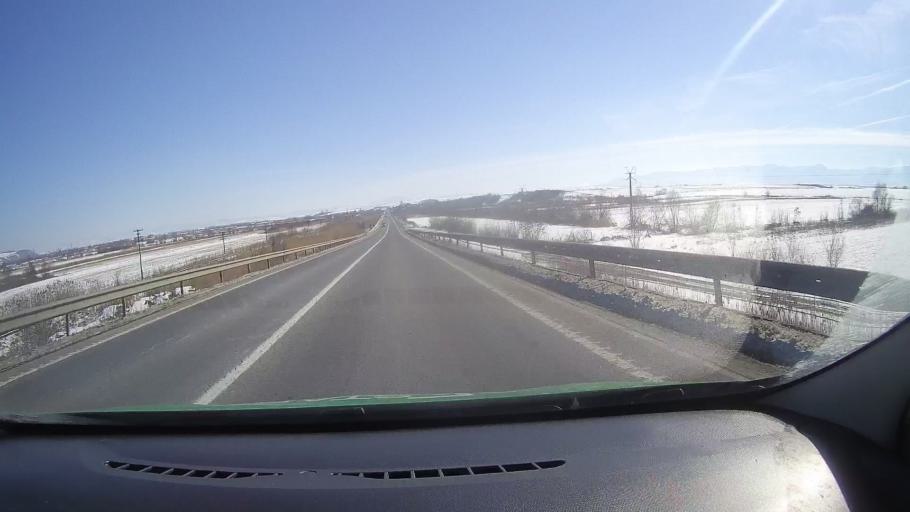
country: RO
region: Brasov
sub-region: Comuna Mandra
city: Mandra
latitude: 45.8307
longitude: 25.0195
